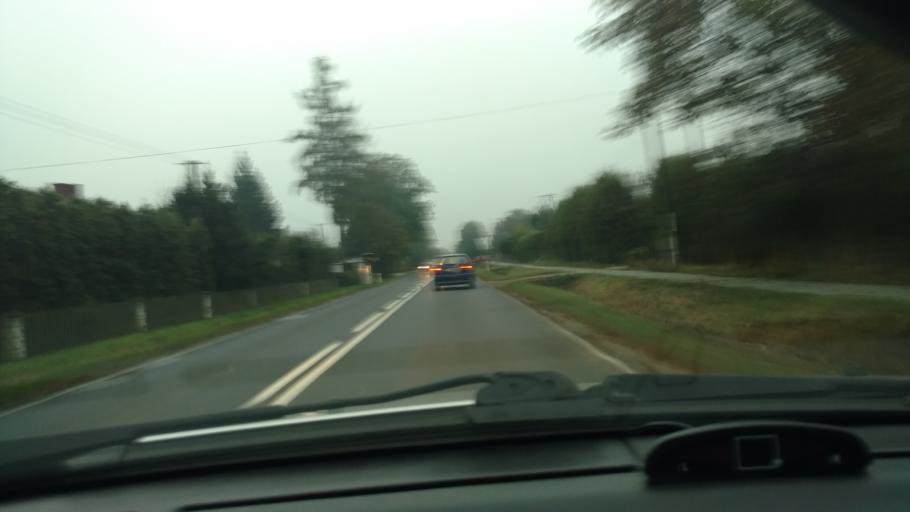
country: PL
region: Subcarpathian Voivodeship
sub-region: Powiat strzyzowski
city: Wysoka Strzyzowska
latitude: 49.8772
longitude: 21.7293
